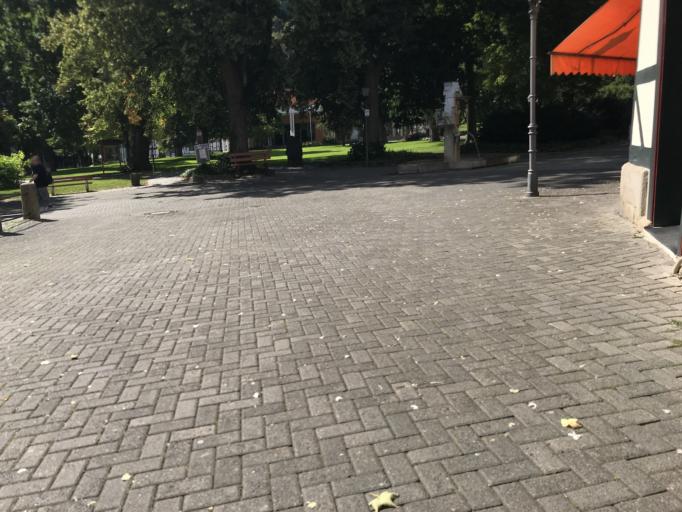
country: DE
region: Hesse
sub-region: Regierungsbezirk Kassel
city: Bad Sooden-Allendorf
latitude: 51.2688
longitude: 9.9650
